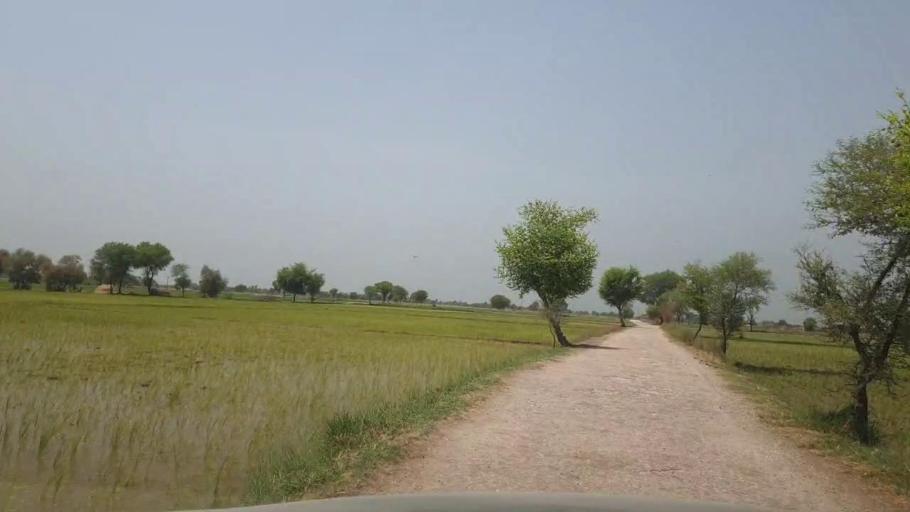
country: PK
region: Sindh
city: Garhi Yasin
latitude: 27.9206
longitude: 68.3702
